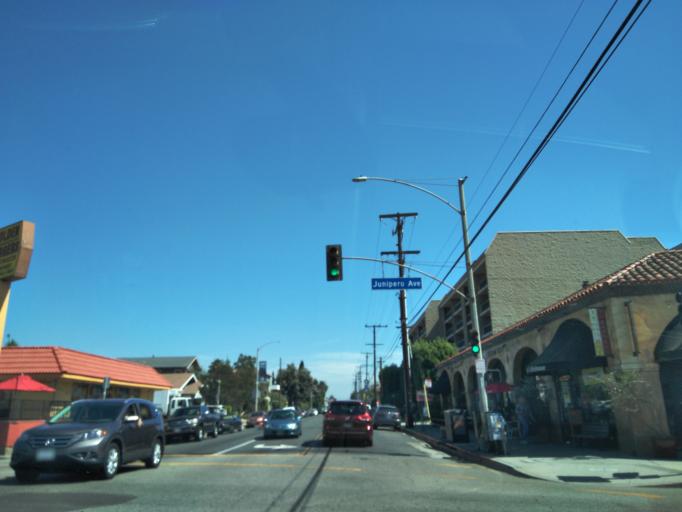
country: US
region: California
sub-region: Los Angeles County
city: Long Beach
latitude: 33.7717
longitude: -118.1645
